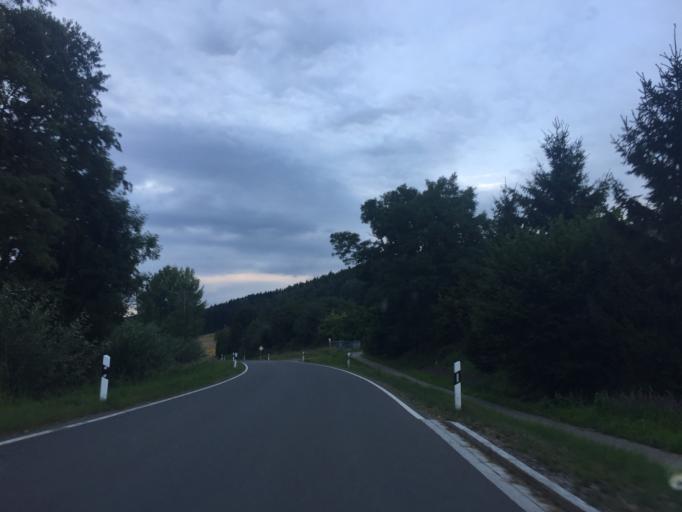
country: DE
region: Bavaria
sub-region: Upper Palatinate
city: Kirchendemenreuth
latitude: 49.7719
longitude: 12.0741
